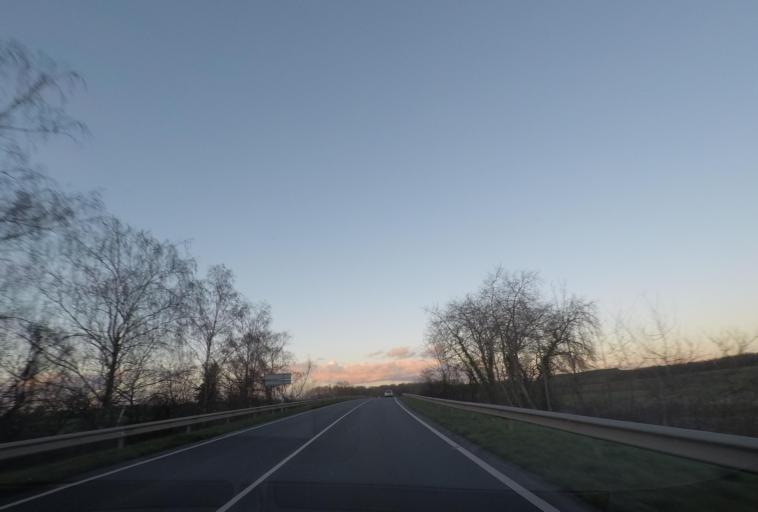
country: FR
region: Ile-de-France
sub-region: Departement de l'Essonne
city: Vert-le-Grand
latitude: 48.5755
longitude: 2.3649
